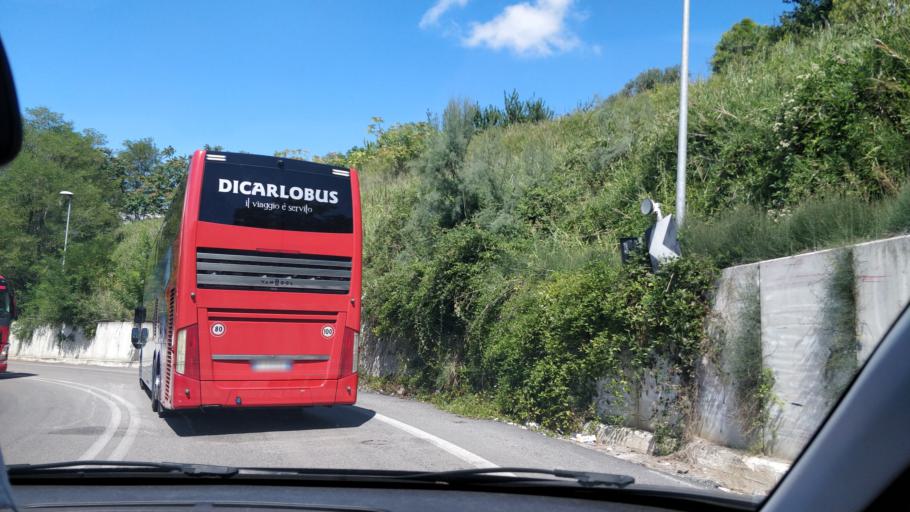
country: IT
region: Abruzzo
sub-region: Provincia di Chieti
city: Francavilla al Mare
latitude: 42.4060
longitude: 14.3033
